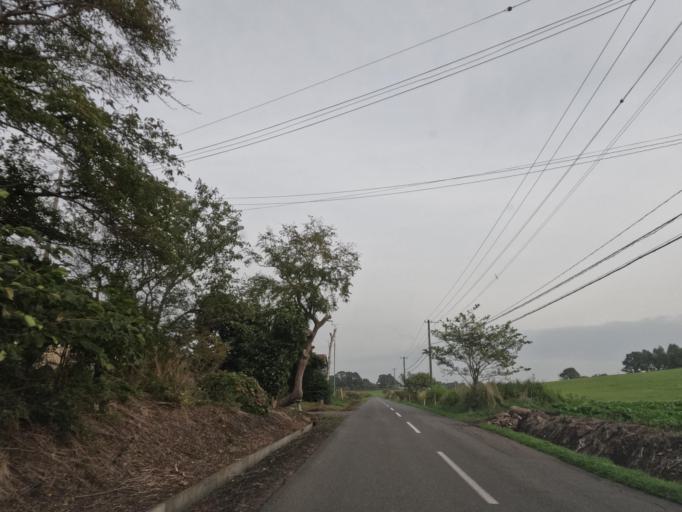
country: JP
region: Hokkaido
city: Date
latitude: 42.4099
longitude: 140.9175
